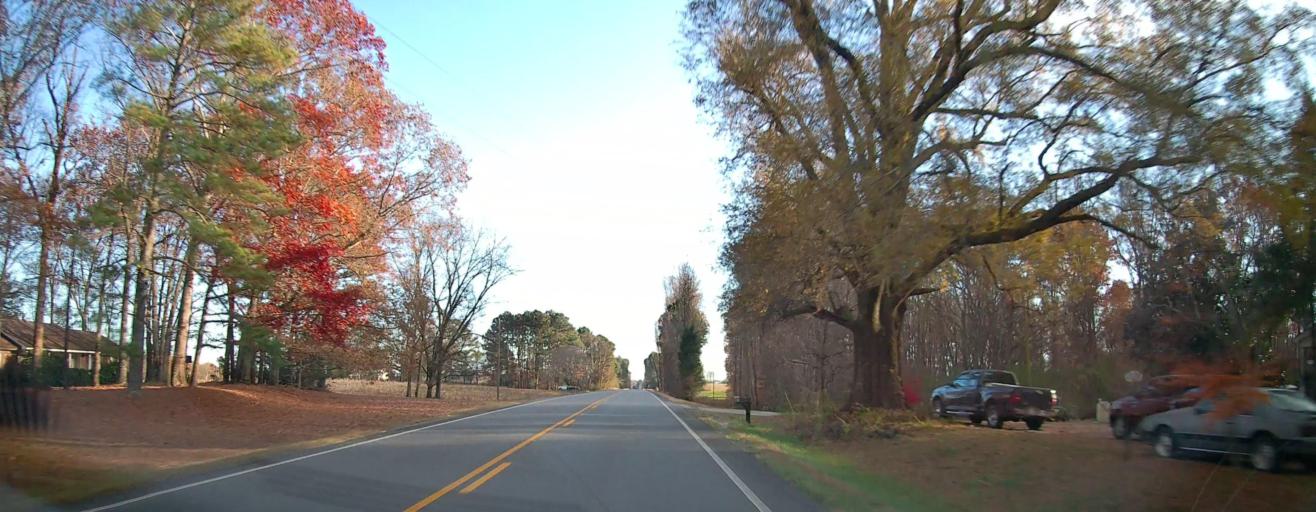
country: US
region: Alabama
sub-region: Marshall County
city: Arab
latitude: 34.2639
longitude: -86.5751
